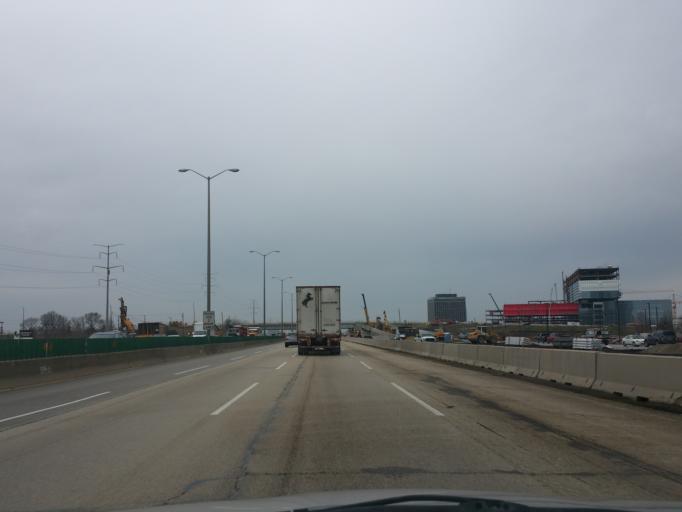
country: US
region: Illinois
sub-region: Cook County
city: Rolling Meadows
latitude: 42.0590
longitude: -88.0398
